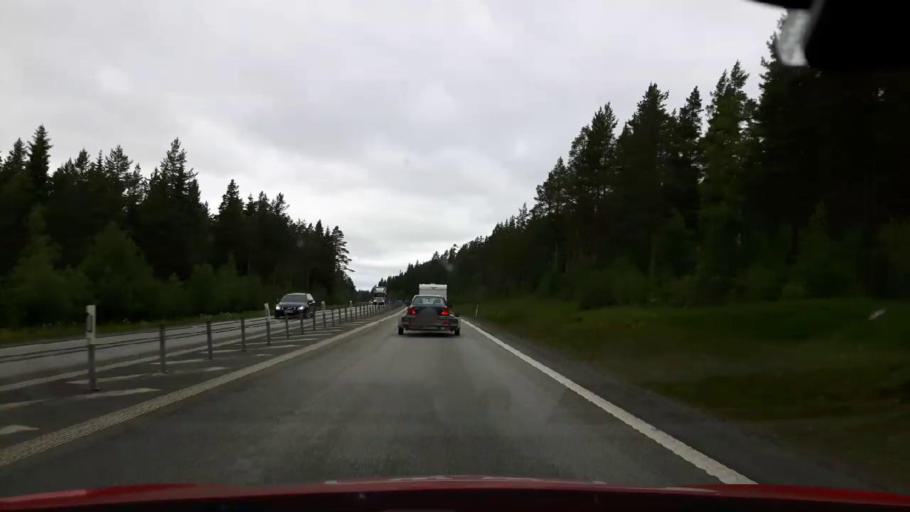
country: SE
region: Jaemtland
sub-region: OEstersunds Kommun
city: Ostersund
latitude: 63.1973
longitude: 14.6858
